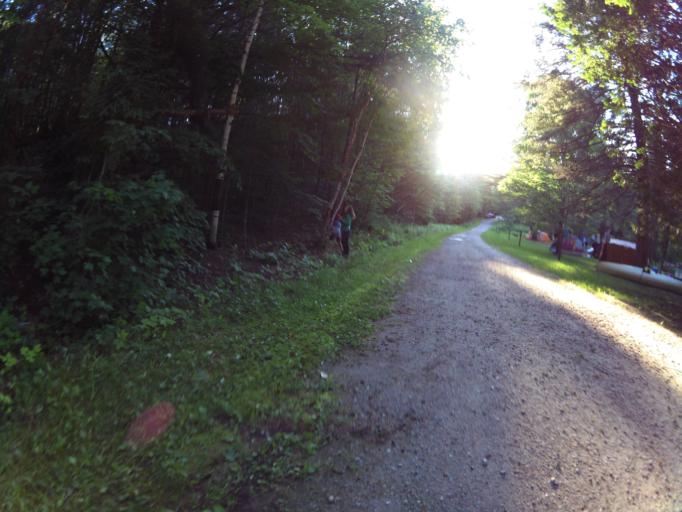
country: CA
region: Quebec
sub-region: Outaouais
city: Wakefield
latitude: 45.5989
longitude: -75.9971
